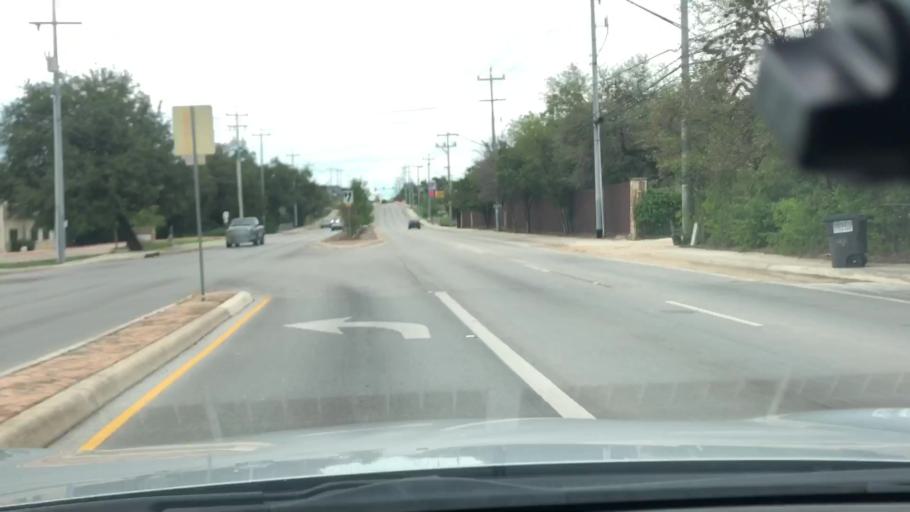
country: US
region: Texas
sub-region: Bexar County
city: Leon Valley
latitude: 29.4994
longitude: -98.6624
